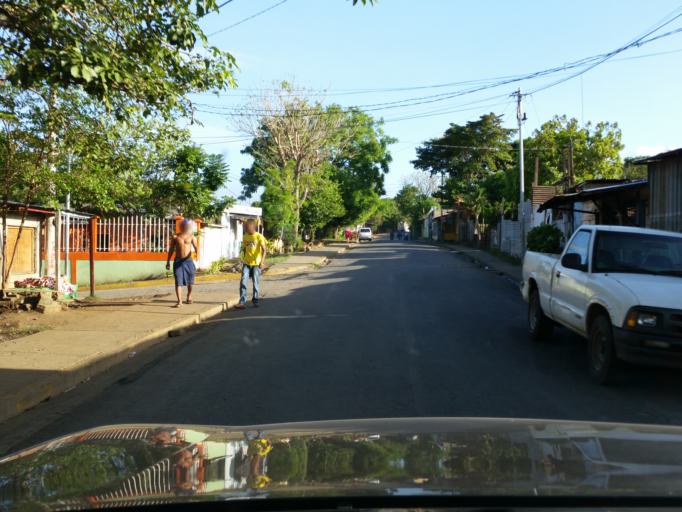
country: NI
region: Managua
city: Managua
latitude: 12.1110
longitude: -86.2902
